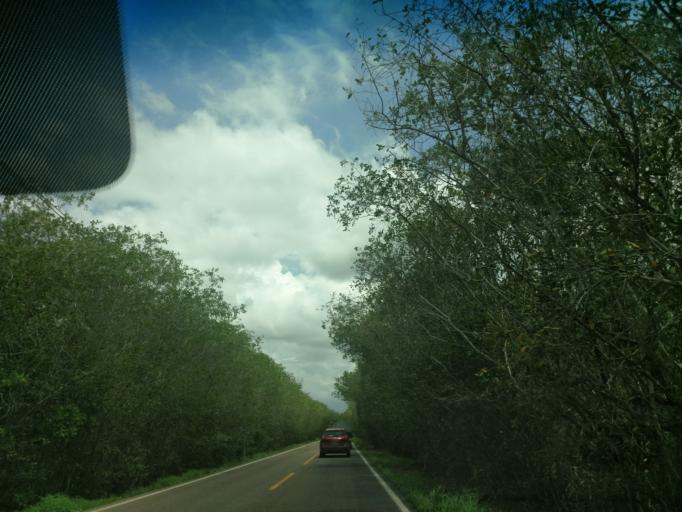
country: MX
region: Nayarit
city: San Blas
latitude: 21.5475
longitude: -105.2532
